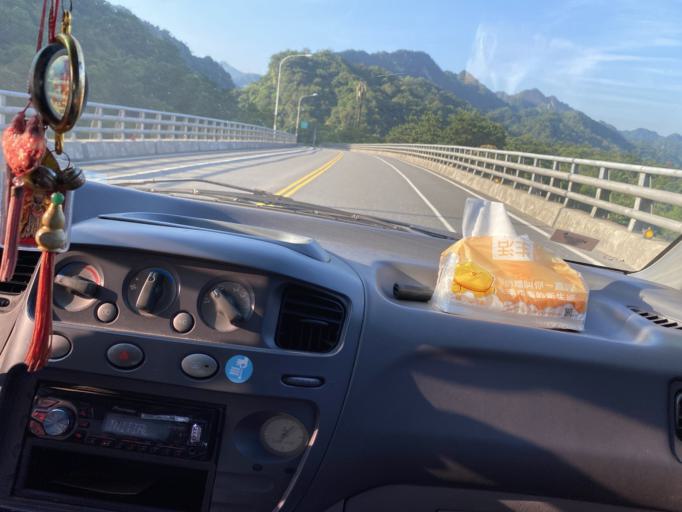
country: TW
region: Taiwan
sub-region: Keelung
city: Keelung
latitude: 25.0423
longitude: 121.7801
